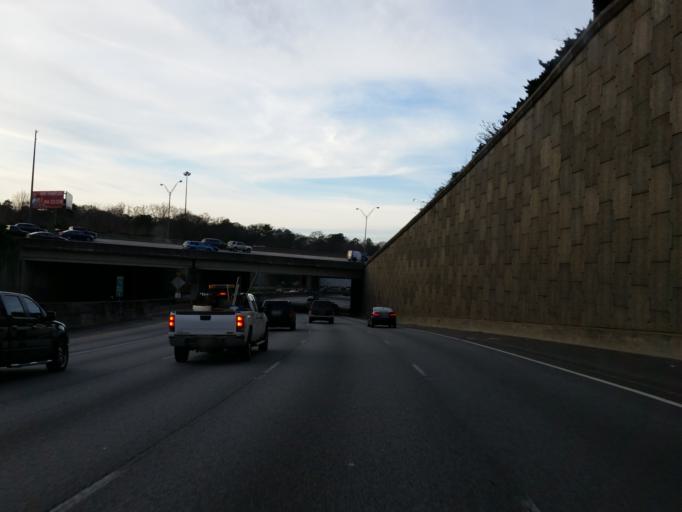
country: US
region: Georgia
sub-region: Fulton County
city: Atlanta
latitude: 33.7956
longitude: -84.3922
